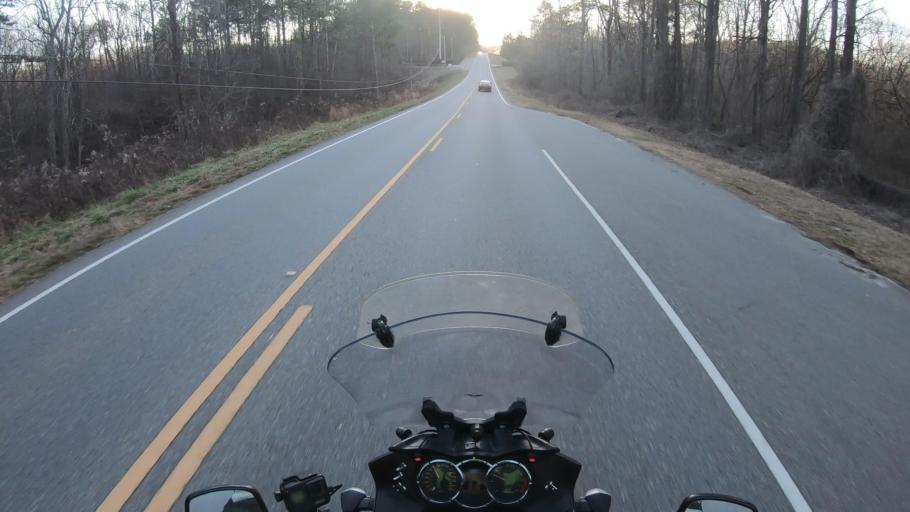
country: US
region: Georgia
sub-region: Dawson County
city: Dawsonville
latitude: 34.3534
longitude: -84.0996
